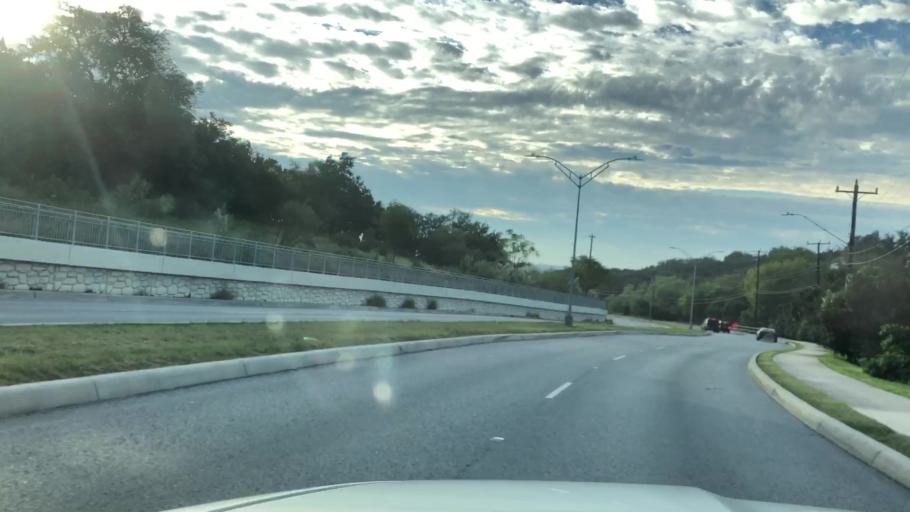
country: US
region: Texas
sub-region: Bexar County
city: Leon Valley
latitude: 29.5435
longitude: -98.6374
